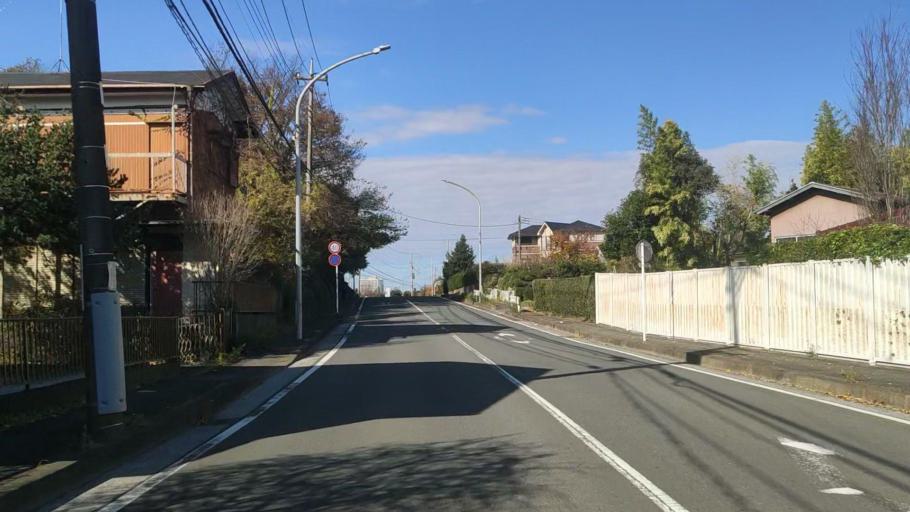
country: JP
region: Kanagawa
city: Yokohama
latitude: 35.4520
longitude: 139.5481
